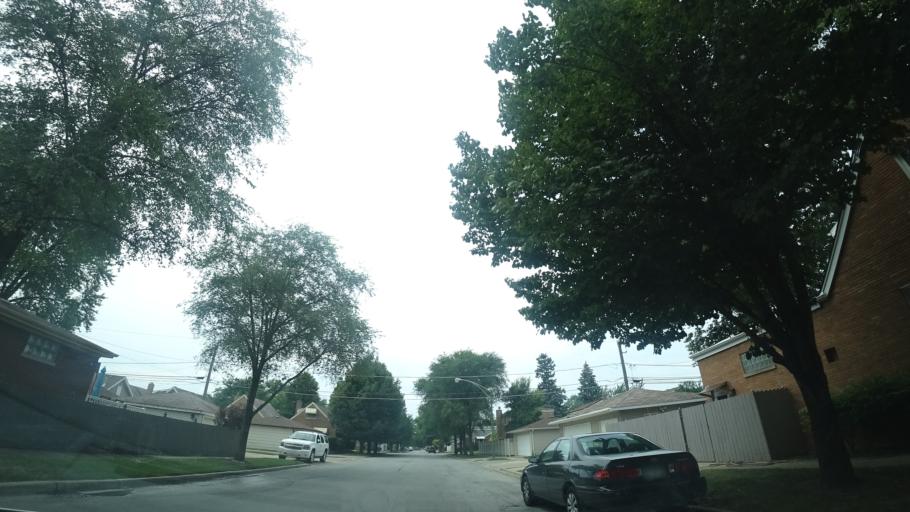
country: US
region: Illinois
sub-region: Cook County
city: Merrionette Park
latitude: 41.6950
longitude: -87.7133
